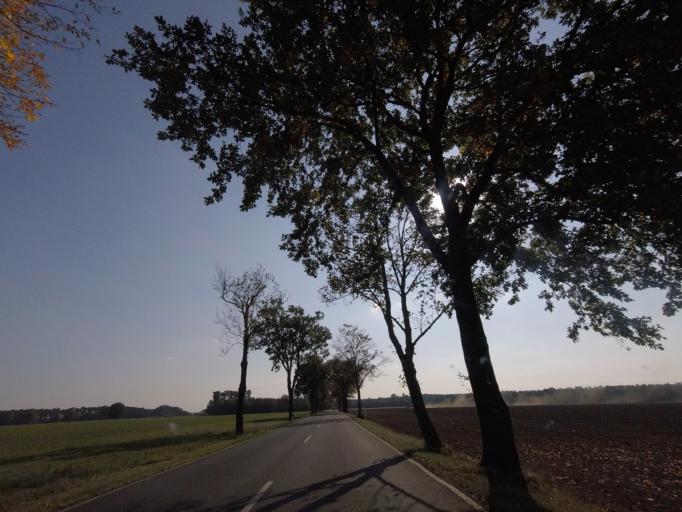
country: DE
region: Saxony-Anhalt
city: Jessen
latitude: 51.8272
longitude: 13.0159
